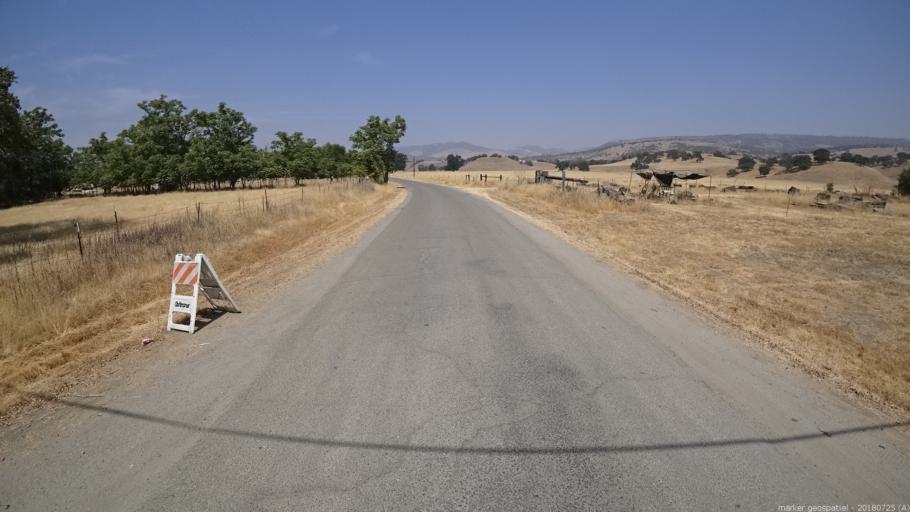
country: US
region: California
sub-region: Fresno County
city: Coalinga
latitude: 35.9010
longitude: -120.4328
